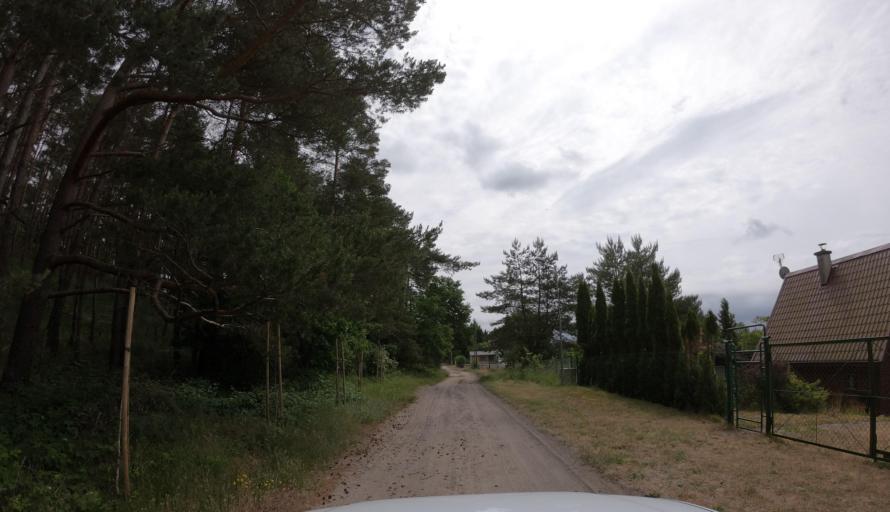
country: PL
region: West Pomeranian Voivodeship
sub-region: Powiat kamienski
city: Wolin
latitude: 53.8590
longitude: 14.5468
